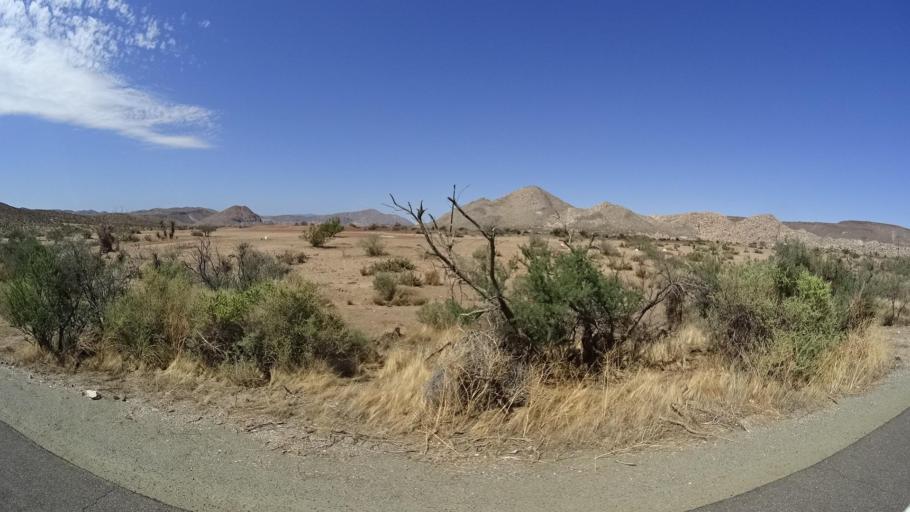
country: MX
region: Baja California
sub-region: Tecate
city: Cereso del Hongo
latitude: 32.6225
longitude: -116.1550
